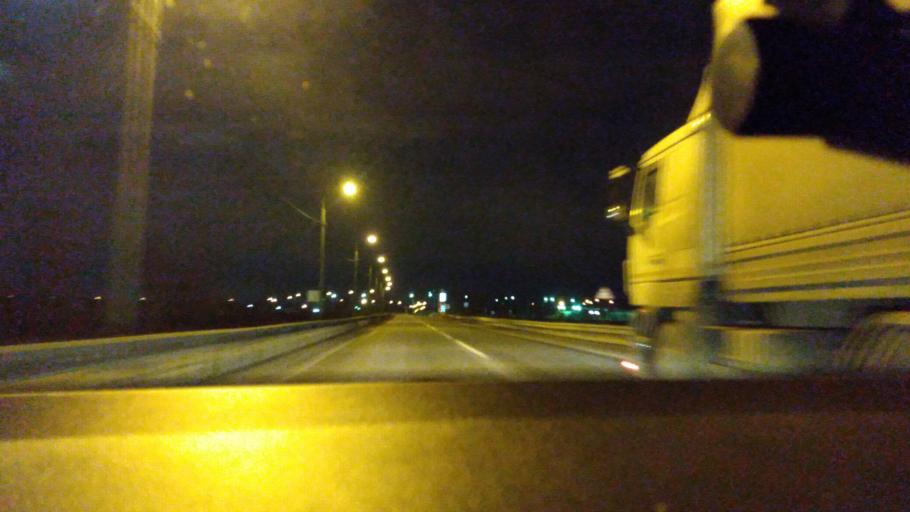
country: RU
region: Moskovskaya
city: Yegor'yevsk
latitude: 55.3916
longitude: 39.0746
